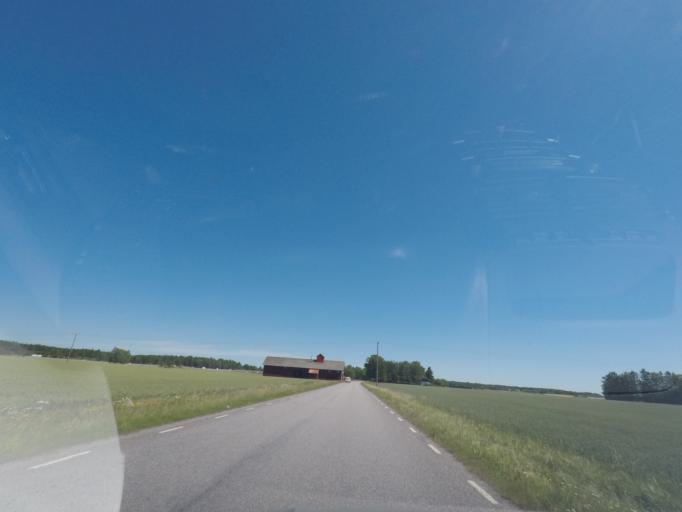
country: SE
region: Uppsala
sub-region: Enkopings Kommun
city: Irsta
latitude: 59.6968
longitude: 16.9822
